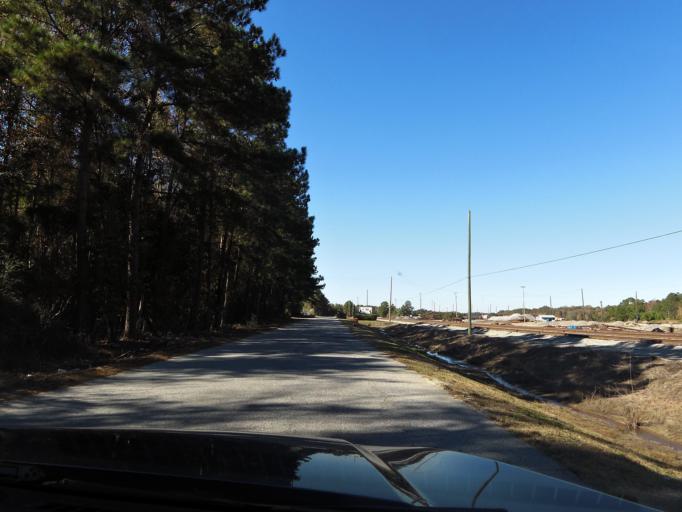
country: US
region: Georgia
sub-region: Chatham County
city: Garden City
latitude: 32.0924
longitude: -81.1597
